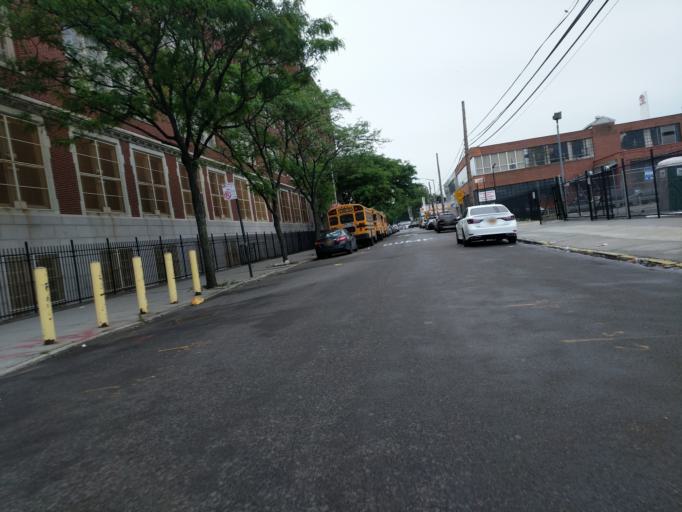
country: US
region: New York
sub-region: Queens County
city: Long Island City
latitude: 40.7527
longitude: -73.9000
